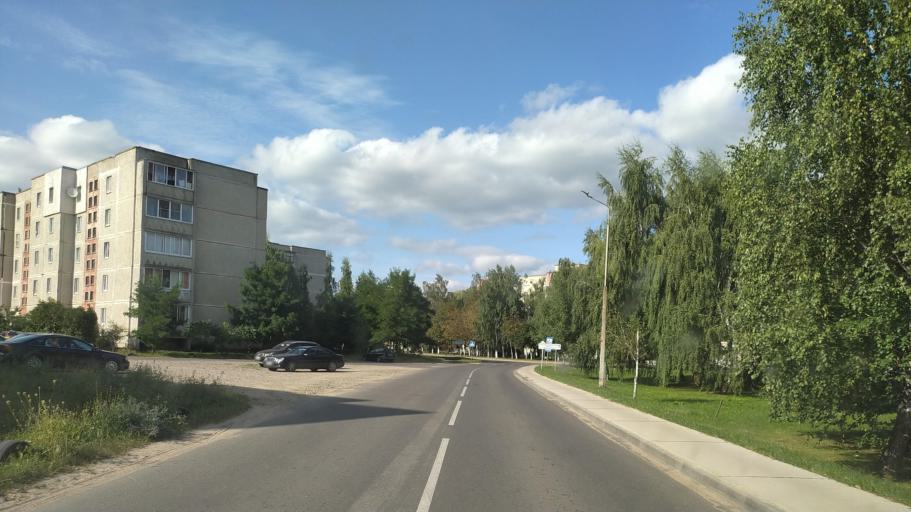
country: BY
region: Brest
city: Byaroza
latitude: 52.5364
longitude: 24.9959
